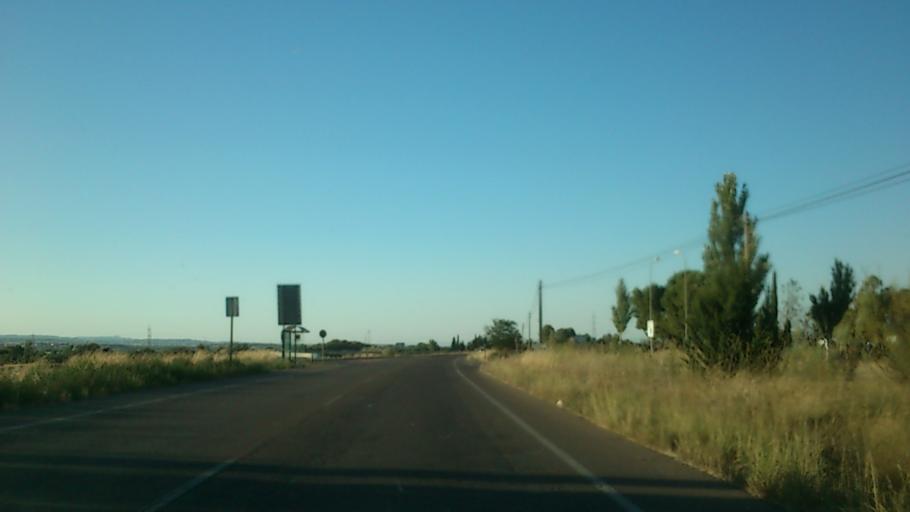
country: ES
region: Aragon
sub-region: Provincia de Zaragoza
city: Villanueva de Gallego
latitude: 41.7342
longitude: -0.8091
